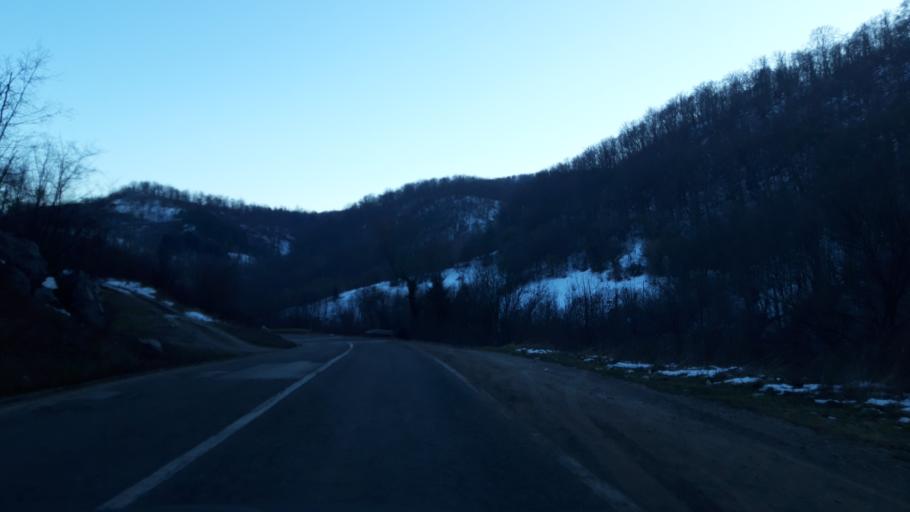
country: BA
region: Republika Srpska
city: Vlasenica
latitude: 44.1824
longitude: 18.9753
